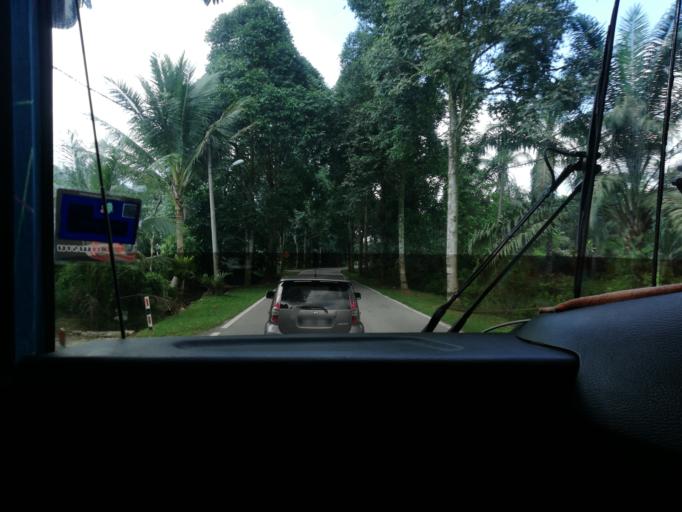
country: MY
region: Kedah
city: Kulim
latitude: 5.2471
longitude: 100.6025
